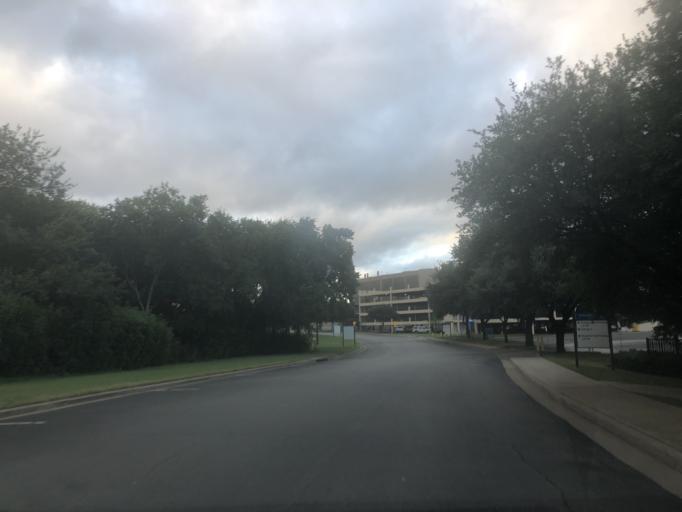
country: US
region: Texas
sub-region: Dallas County
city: Dallas
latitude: 32.8135
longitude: -96.8449
